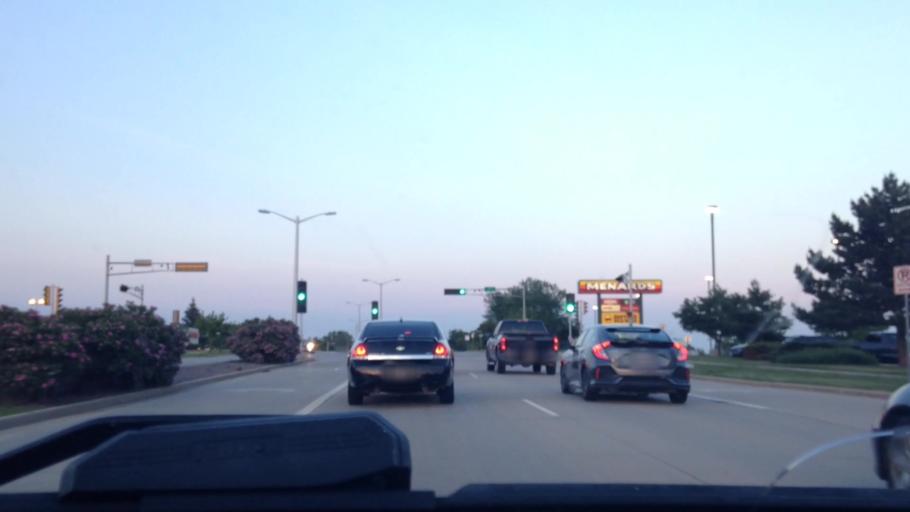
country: US
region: Wisconsin
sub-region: Washington County
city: West Bend
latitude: 43.3977
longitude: -88.1849
